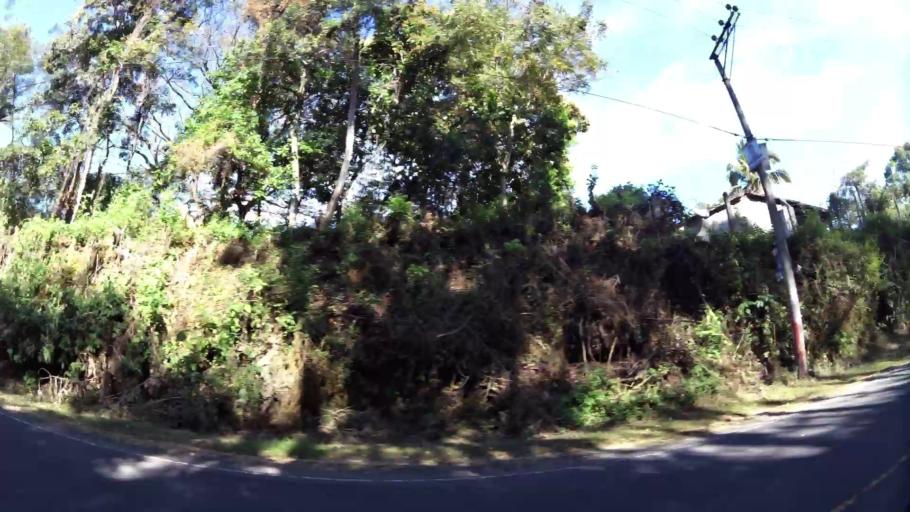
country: SV
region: Cuscatlan
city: Tenancingo
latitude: 13.8431
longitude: -89.0276
